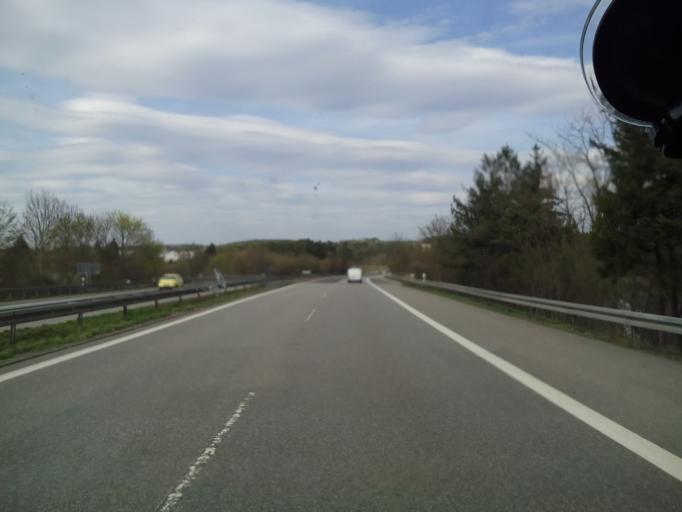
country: DE
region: Bavaria
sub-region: Regierungsbezirk Mittelfranken
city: Roth
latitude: 49.2397
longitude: 11.1042
